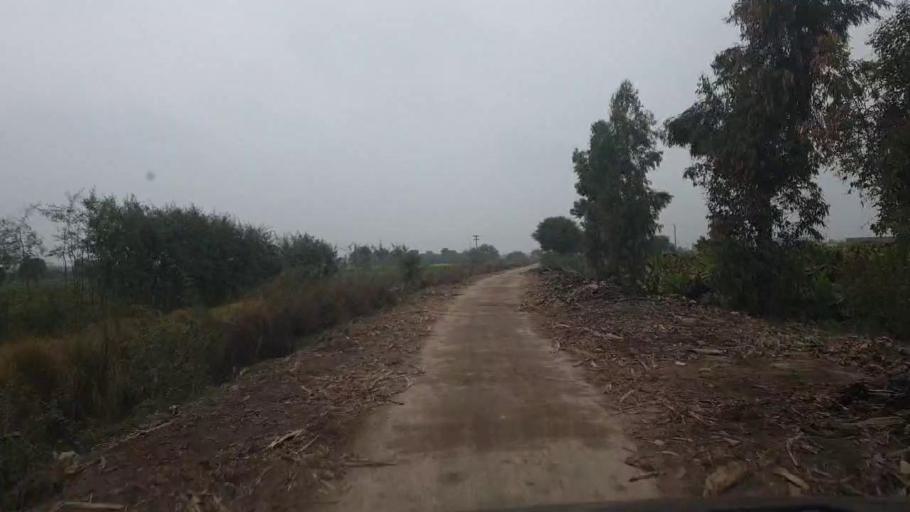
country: PK
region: Sindh
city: Tando Adam
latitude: 25.8498
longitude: 68.6758
